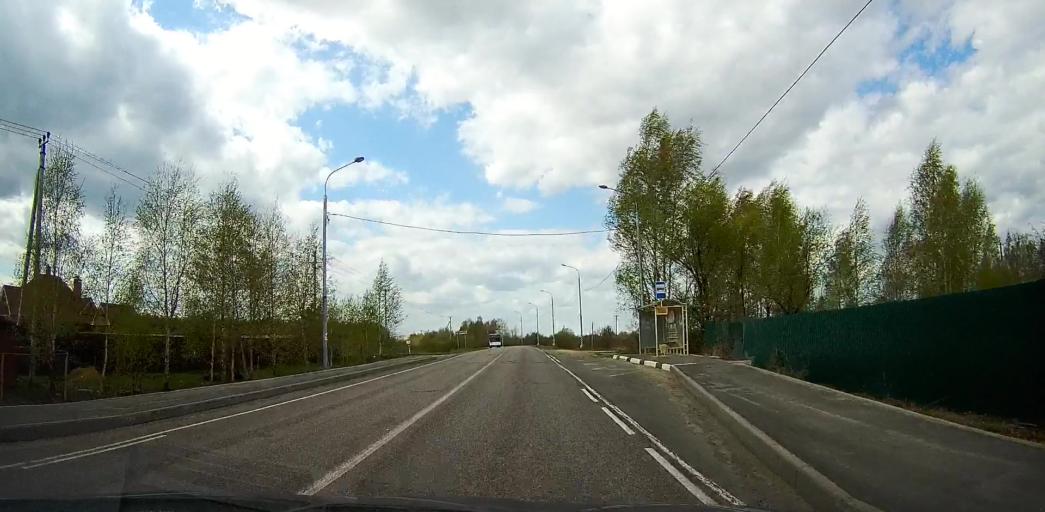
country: RU
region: Moskovskaya
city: Davydovo
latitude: 55.6651
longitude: 38.7996
